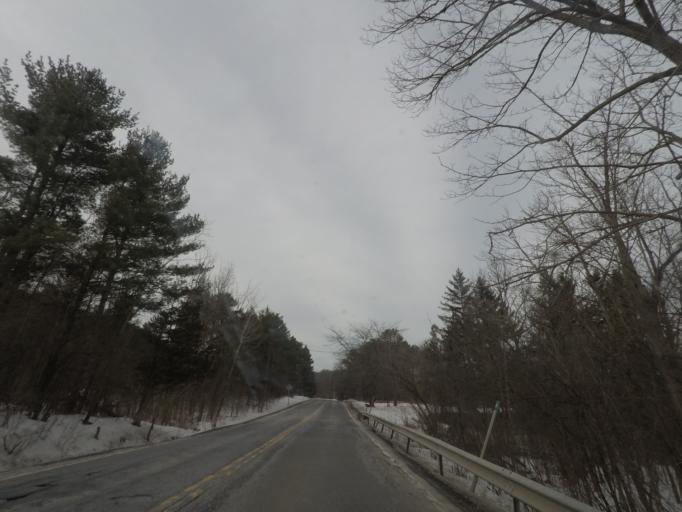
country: US
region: New York
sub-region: Albany County
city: Altamont
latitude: 42.6686
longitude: -74.0058
